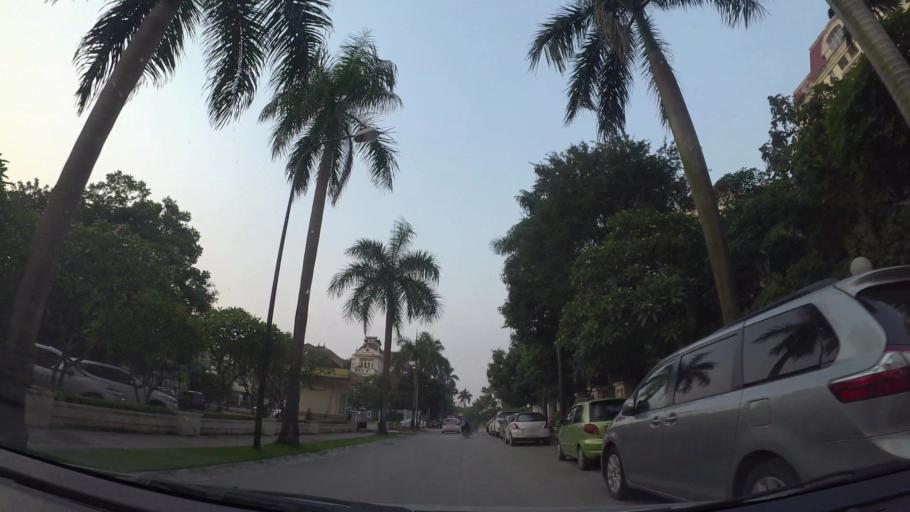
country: VN
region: Ha Noi
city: Tay Ho
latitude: 21.0721
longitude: 105.8081
